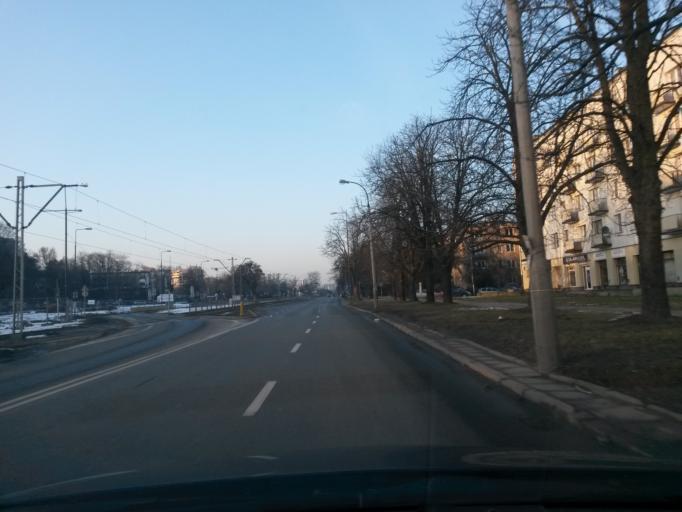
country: PL
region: Masovian Voivodeship
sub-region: Warszawa
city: Ochota
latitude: 52.1965
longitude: 21.0021
